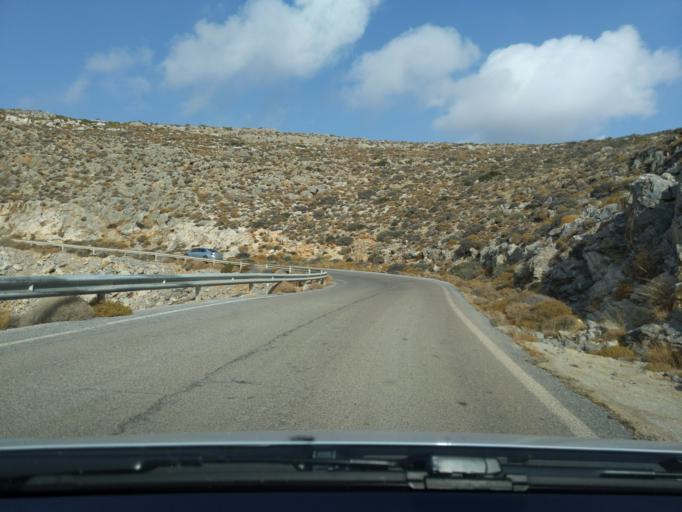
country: GR
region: Crete
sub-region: Nomos Lasithiou
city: Palekastro
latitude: 35.0846
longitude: 26.2616
